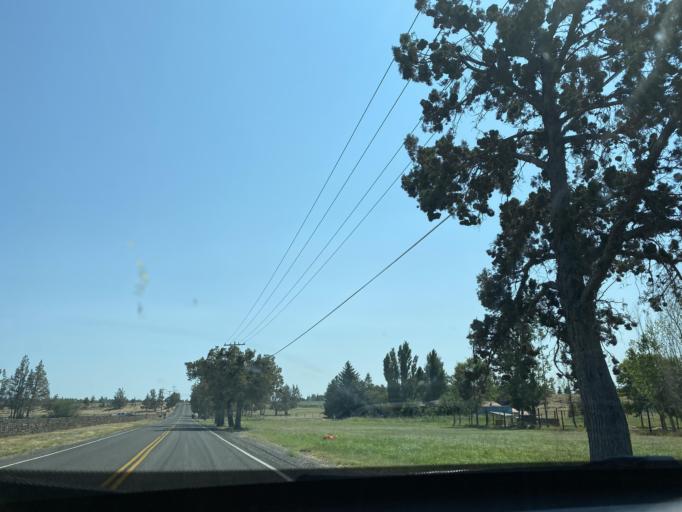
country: US
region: Oregon
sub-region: Deschutes County
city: Terrebonne
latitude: 44.3648
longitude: -121.1586
